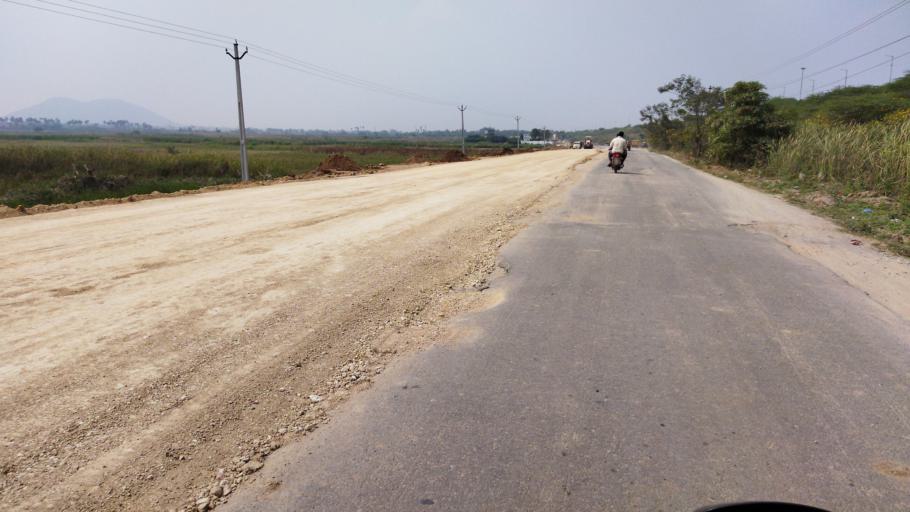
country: IN
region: Telangana
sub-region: Nalgonda
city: Nalgonda
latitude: 17.0782
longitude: 79.3095
